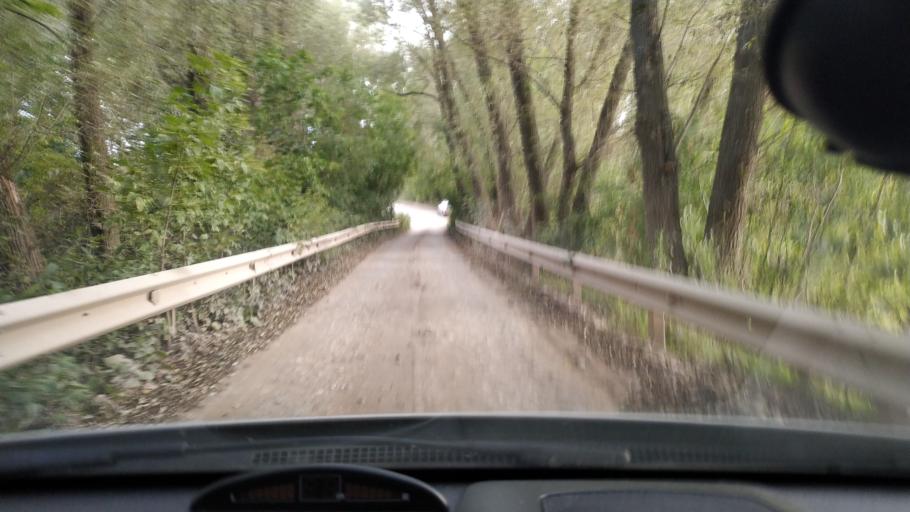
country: RU
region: Rjazan
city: Polyany
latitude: 54.5621
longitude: 39.8750
